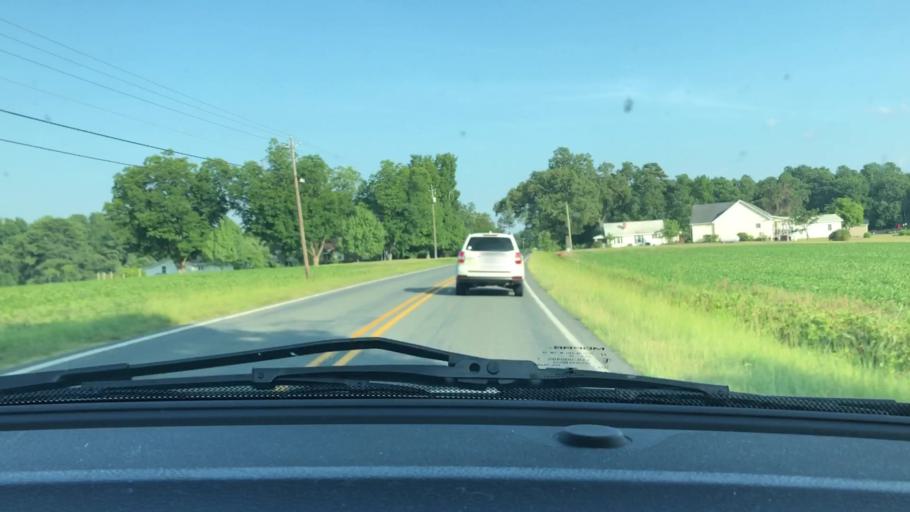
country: US
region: North Carolina
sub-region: Lee County
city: Broadway
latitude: 35.3558
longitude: -79.0782
